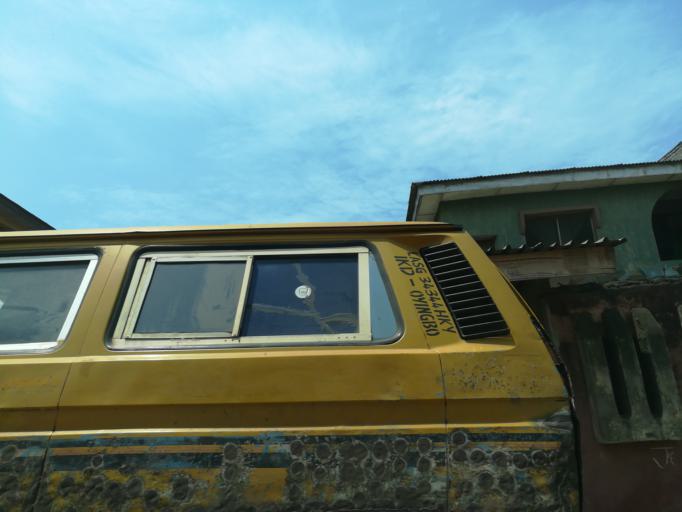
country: NG
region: Lagos
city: Ikorodu
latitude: 6.6215
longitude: 3.4972
